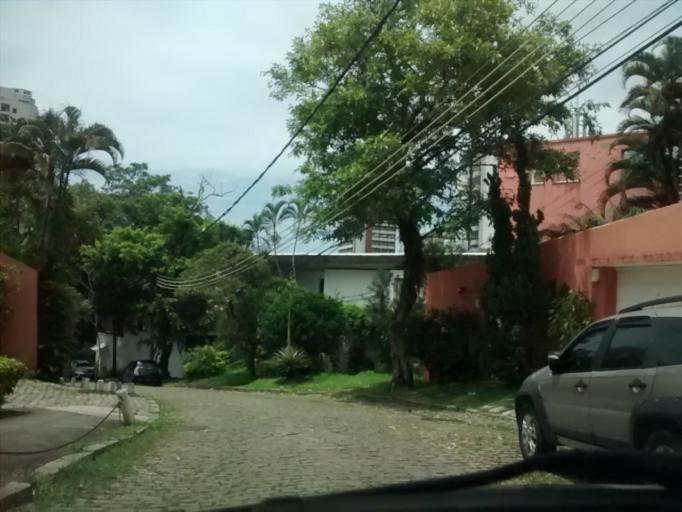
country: BR
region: Rio de Janeiro
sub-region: Rio De Janeiro
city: Rio de Janeiro
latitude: -22.9971
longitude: -43.2690
